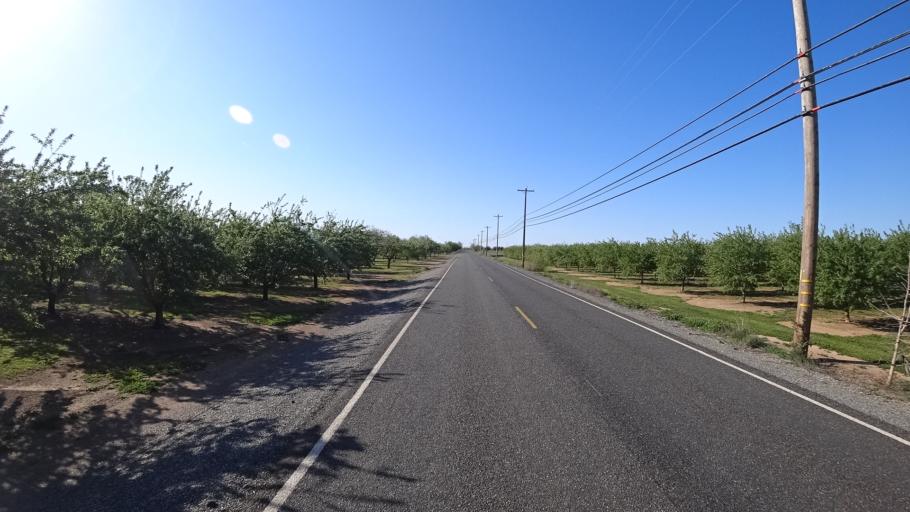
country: US
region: California
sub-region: Glenn County
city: Hamilton City
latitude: 39.7733
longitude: -122.1042
